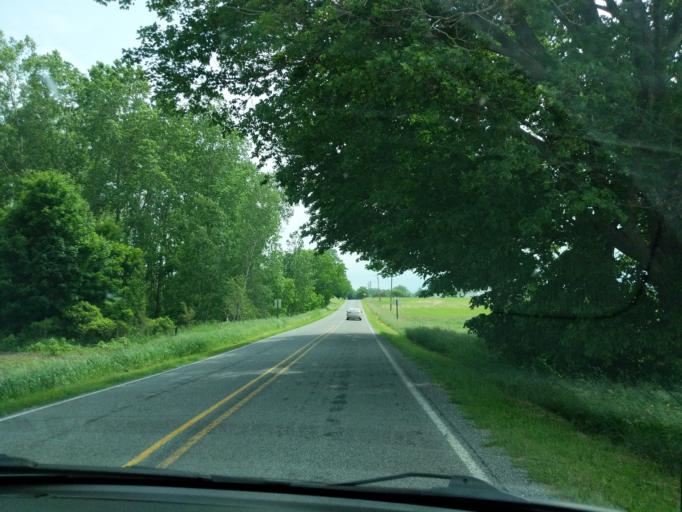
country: US
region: Michigan
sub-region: Ingham County
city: Williamston
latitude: 42.6933
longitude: -84.2256
